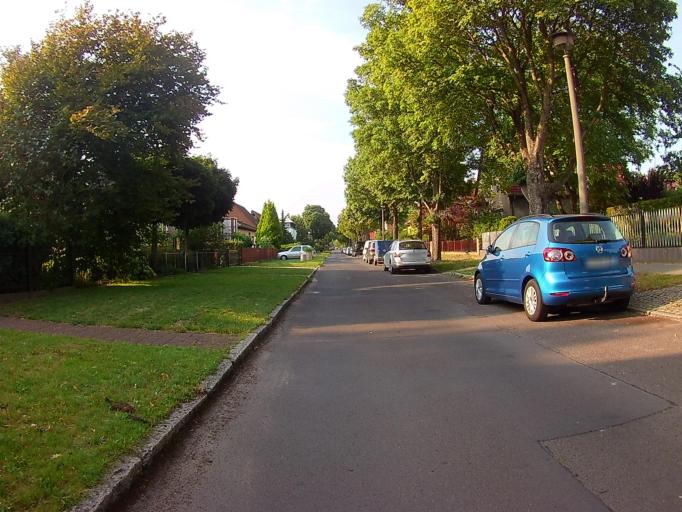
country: DE
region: Berlin
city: Biesdorf
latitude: 52.5219
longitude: 13.5491
